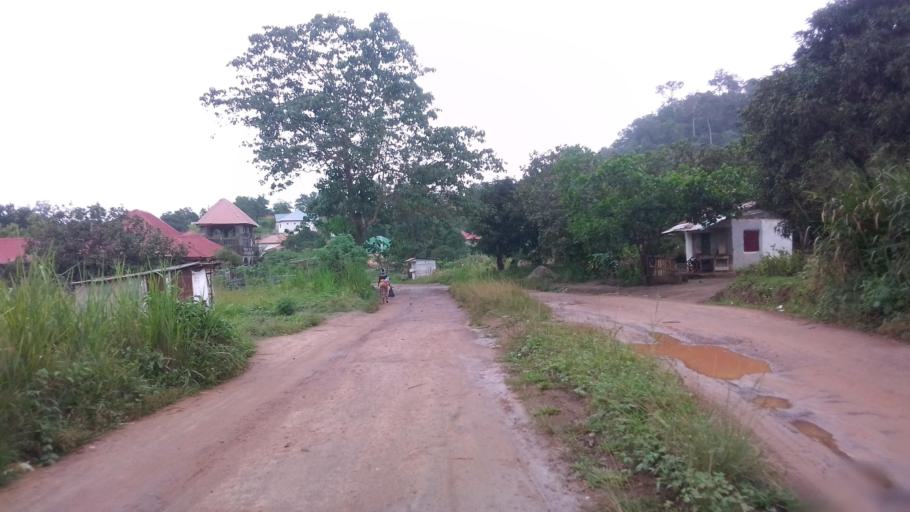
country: SL
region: Eastern Province
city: Kenema
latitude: 7.8481
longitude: -11.2140
